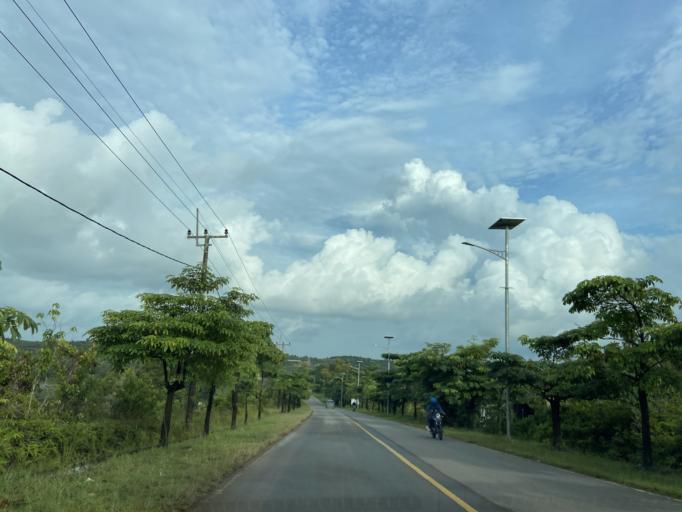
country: ID
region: Riau Islands
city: Tanjungpinang
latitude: 0.9350
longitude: 104.1058
